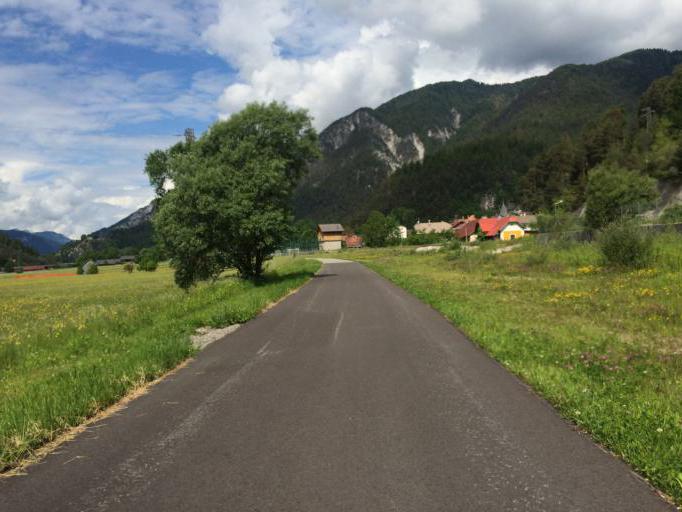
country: IT
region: Friuli Venezia Giulia
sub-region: Provincia di Udine
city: Malborghetto
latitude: 46.5093
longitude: 13.4789
